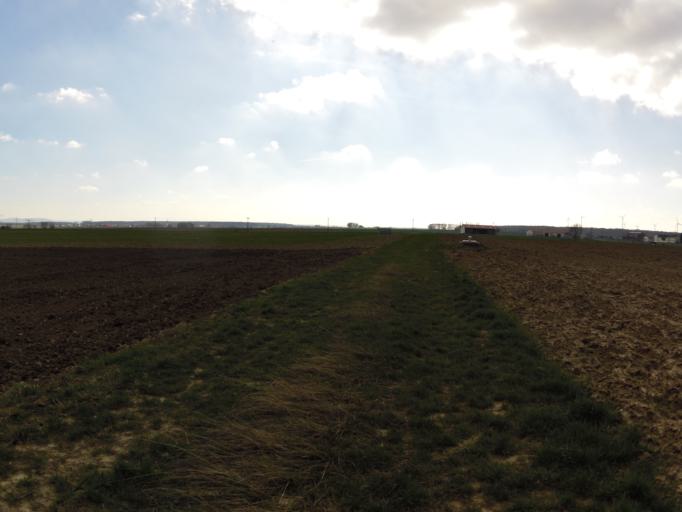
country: DE
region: Bavaria
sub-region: Regierungsbezirk Unterfranken
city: Biebelried
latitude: 49.7475
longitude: 10.0730
